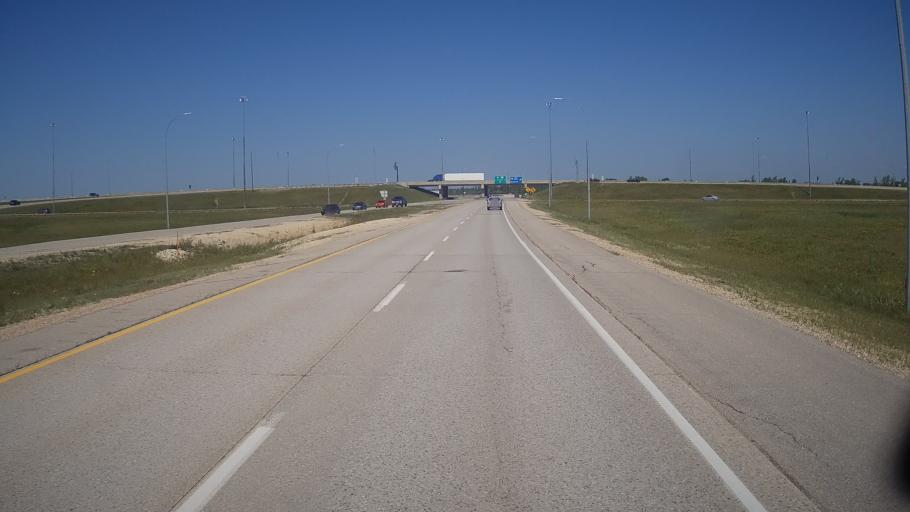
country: CA
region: Manitoba
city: Winnipeg
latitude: 49.8330
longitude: -96.9594
